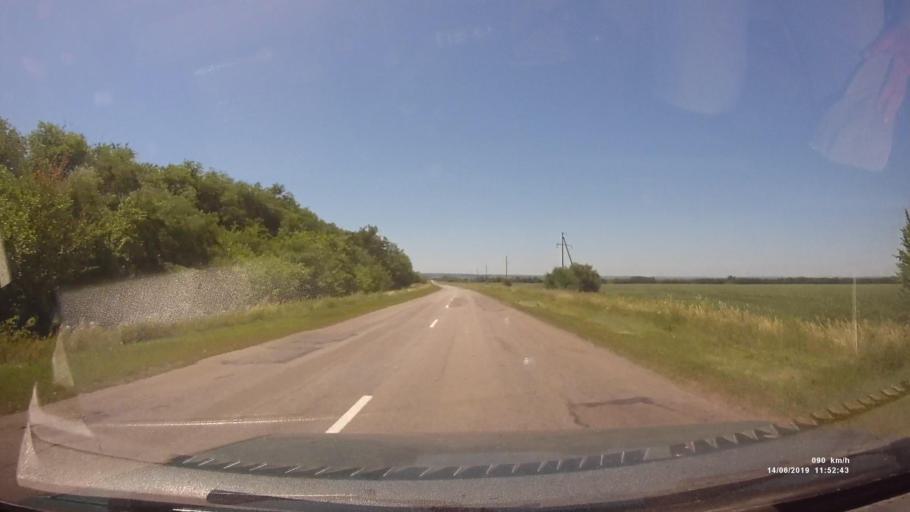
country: RU
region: Rostov
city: Kazanskaya
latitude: 49.8336
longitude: 41.2239
